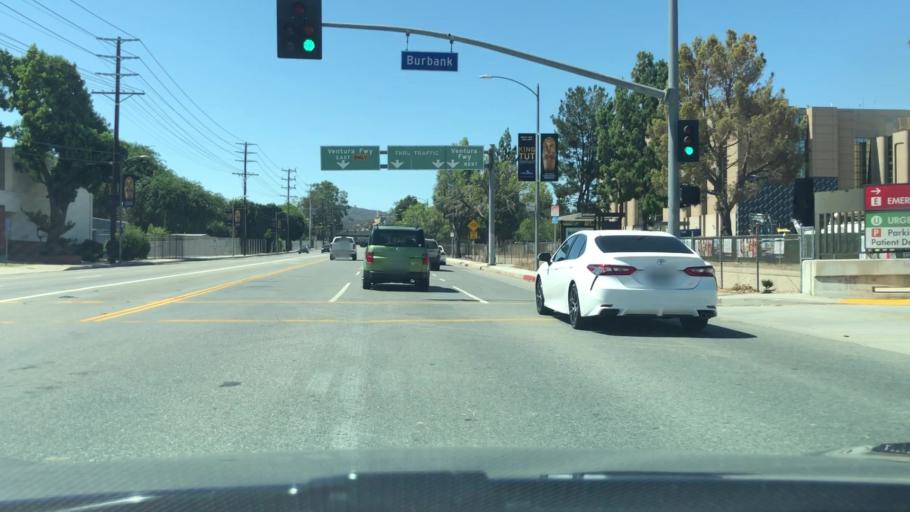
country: US
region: California
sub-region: Los Angeles County
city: Woodland Hills
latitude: 34.1720
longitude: -118.5882
